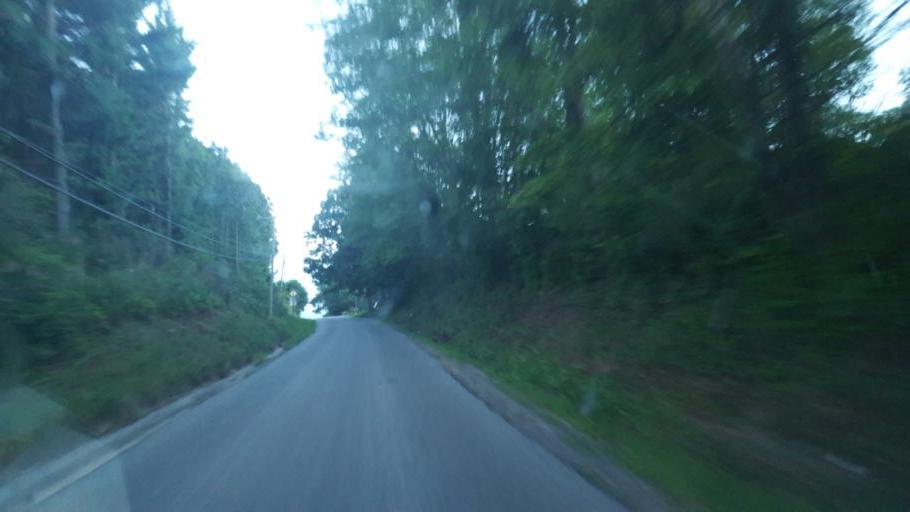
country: US
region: Pennsylvania
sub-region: Clarion County
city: Knox
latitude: 41.2271
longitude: -79.5394
